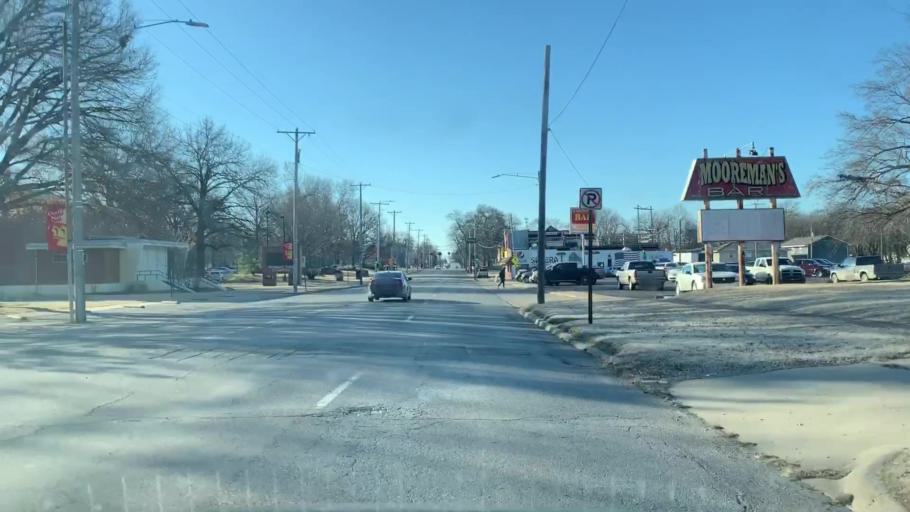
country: US
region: Kansas
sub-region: Crawford County
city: Pittsburg
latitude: 37.3933
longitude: -94.7051
